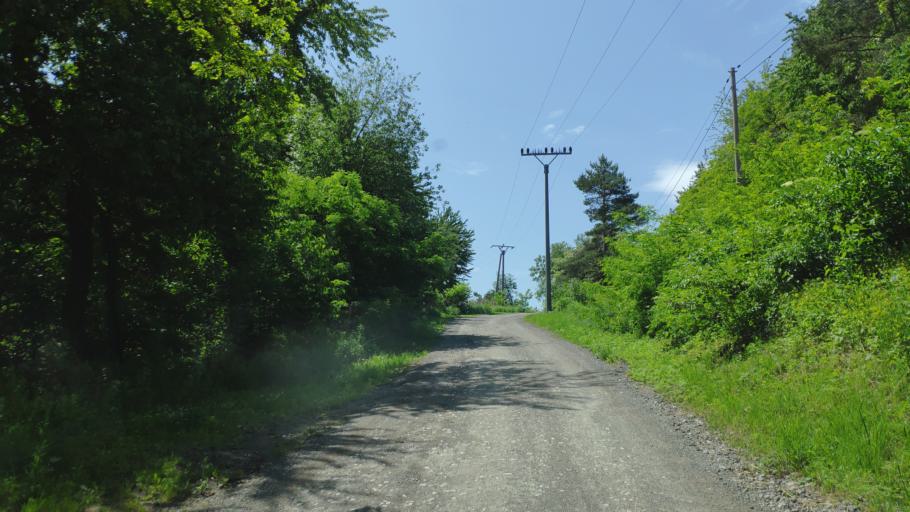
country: SK
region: Kosicky
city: Medzev
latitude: 48.7165
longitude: 20.9838
